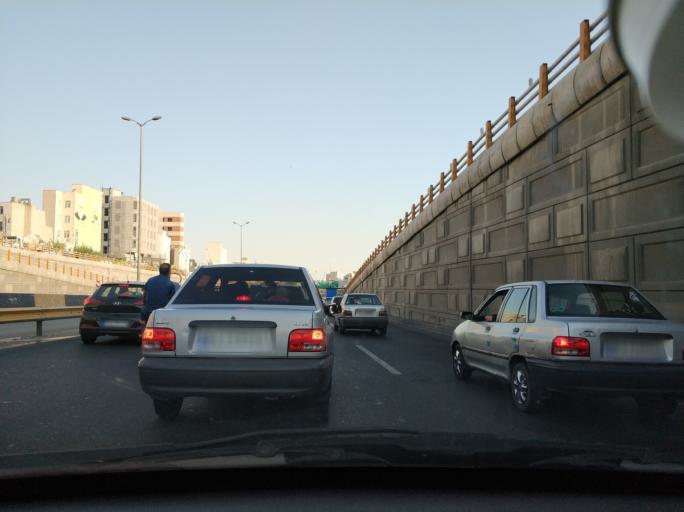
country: IR
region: Tehran
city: Tehran
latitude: 35.6926
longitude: 51.4568
